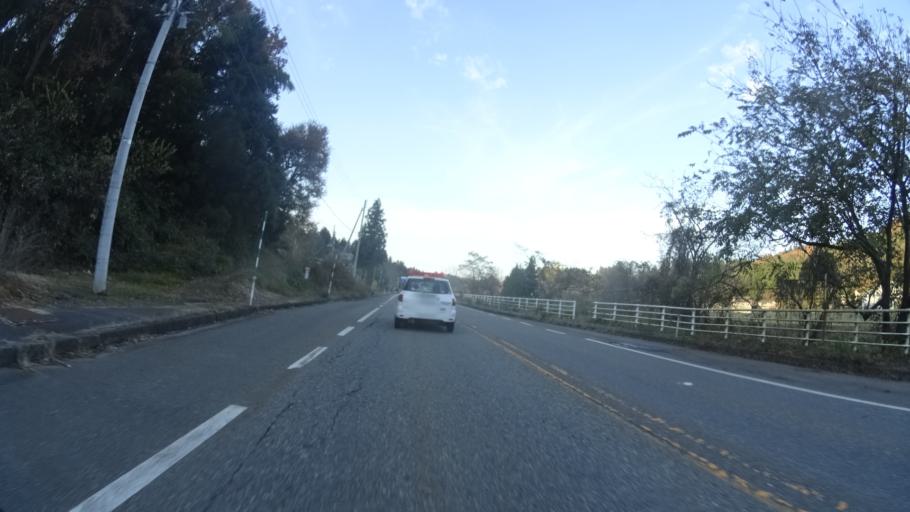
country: JP
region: Niigata
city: Nagaoka
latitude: 37.4235
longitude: 138.7263
